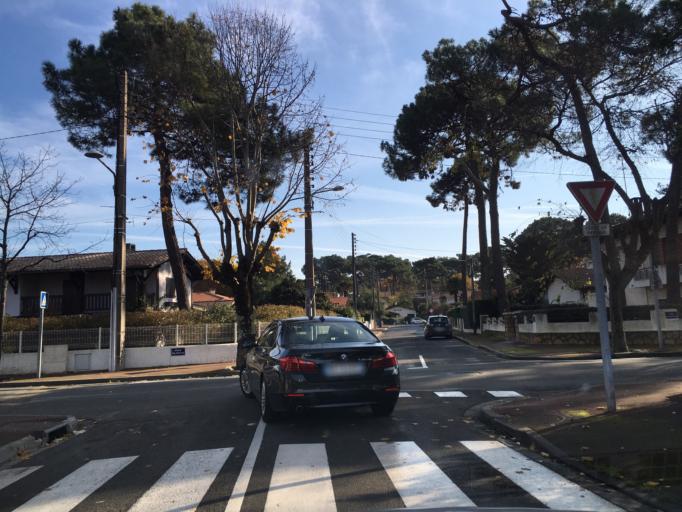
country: FR
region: Aquitaine
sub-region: Departement de la Gironde
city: Arcachon
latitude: 44.6514
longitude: -1.1845
